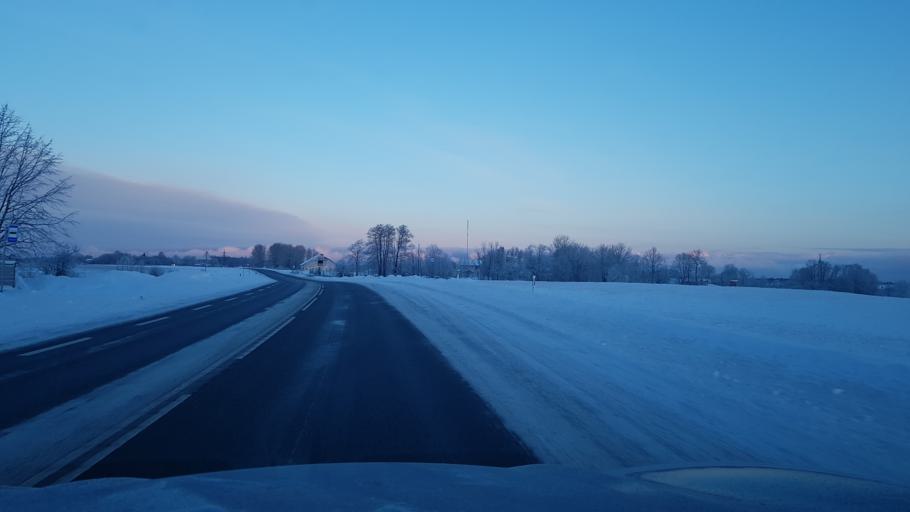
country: EE
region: Ida-Virumaa
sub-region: Narva-Joesuu linn
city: Narva-Joesuu
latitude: 59.3966
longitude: 28.0779
